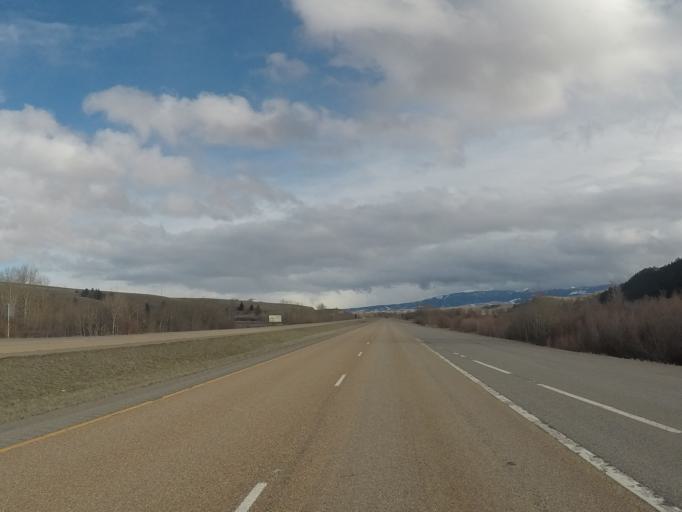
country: US
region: Montana
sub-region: Granite County
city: Philipsburg
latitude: 46.6902
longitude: -113.2005
